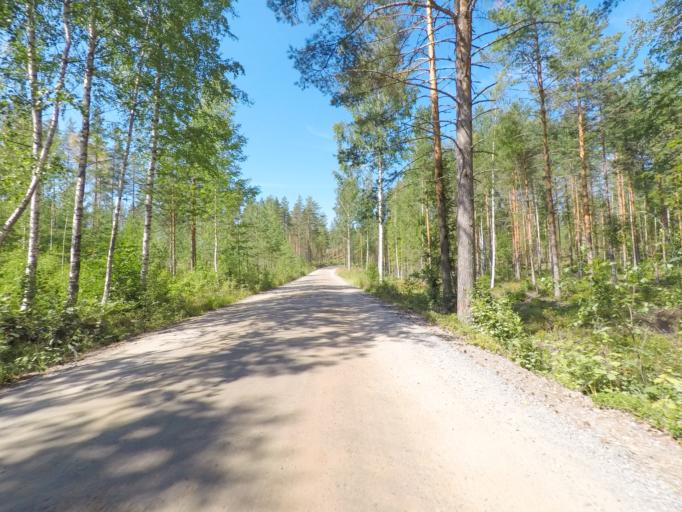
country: FI
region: Southern Savonia
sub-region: Mikkeli
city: Puumala
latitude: 61.4142
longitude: 28.0468
